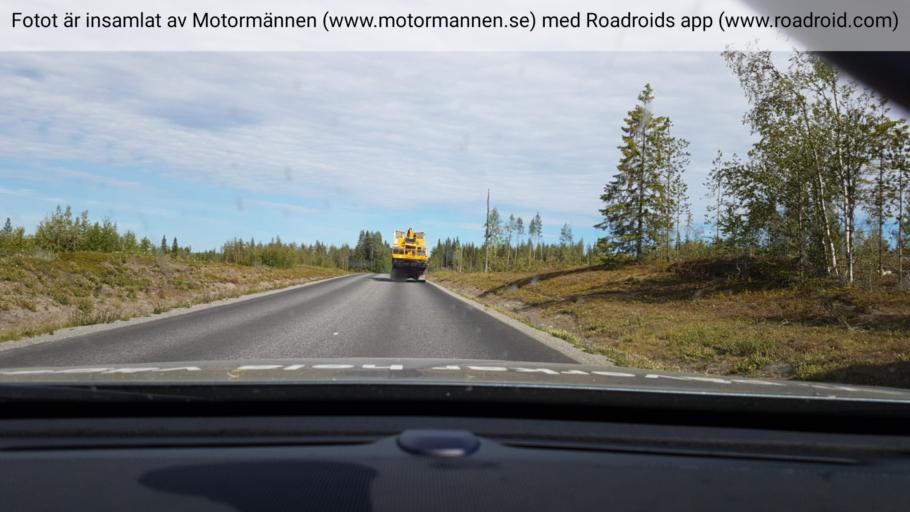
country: SE
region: Vaesterbotten
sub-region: Lycksele Kommun
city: Soderfors
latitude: 64.8307
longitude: 18.0149
